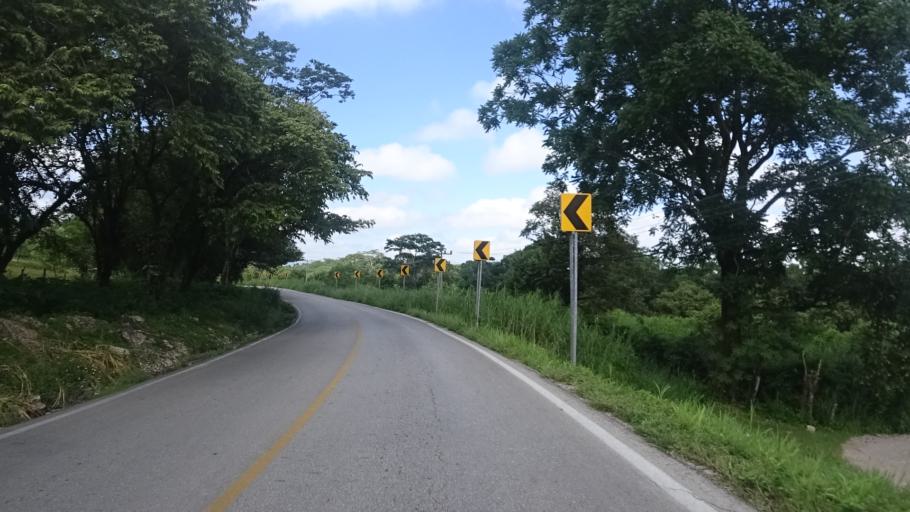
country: MX
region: Chiapas
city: Palenque
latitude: 17.4836
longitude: -91.9681
